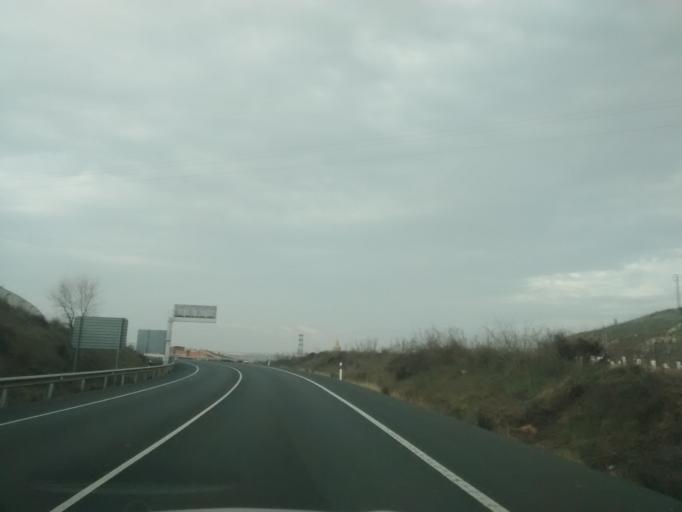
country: ES
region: La Rioja
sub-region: Provincia de La Rioja
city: Cenicero
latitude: 42.4764
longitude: -2.6430
